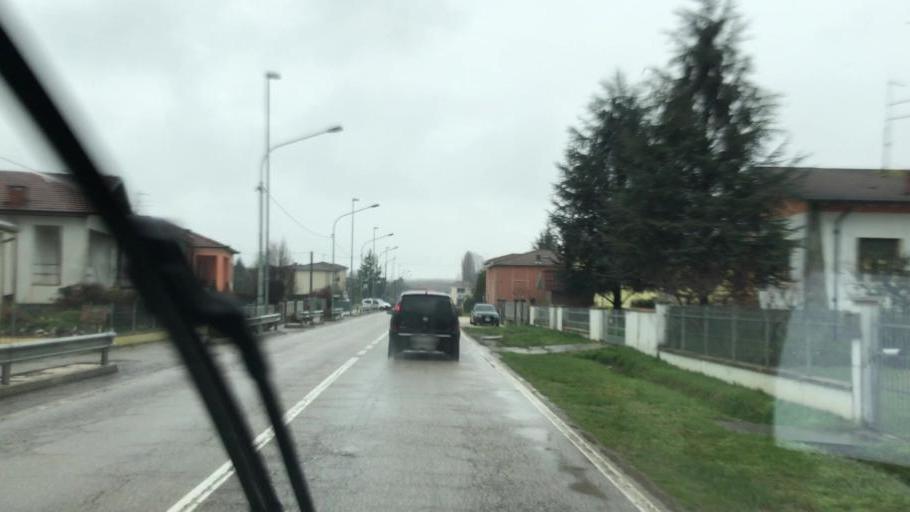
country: IT
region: Lombardy
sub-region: Provincia di Mantova
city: Borgofranco sul Po
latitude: 45.0477
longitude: 11.2075
